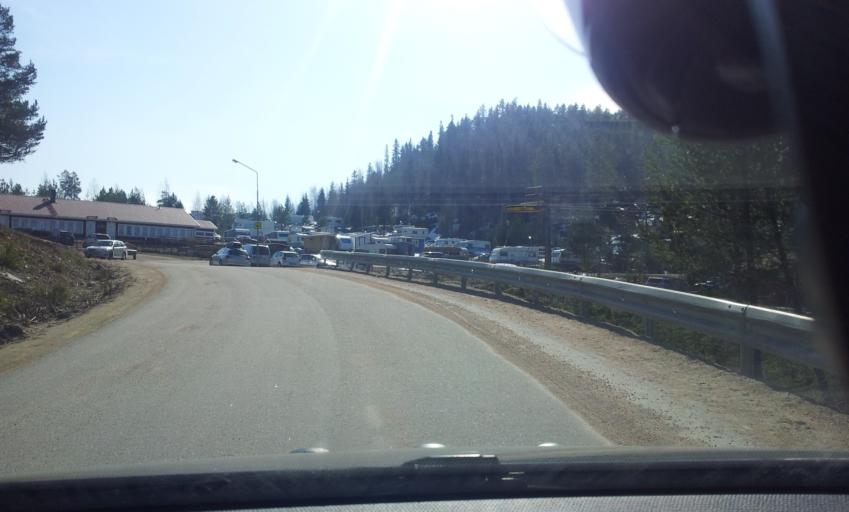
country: SE
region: Gaevleborg
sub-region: Ljusdals Kommun
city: Jaervsoe
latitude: 61.7228
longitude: 16.1592
